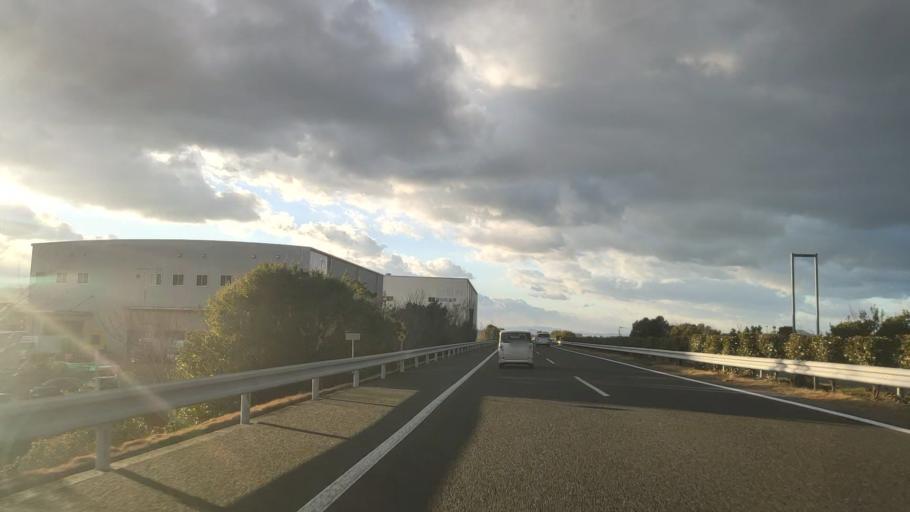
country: JP
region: Ehime
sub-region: Shikoku-chuo Shi
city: Matsuyama
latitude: 33.7863
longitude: 132.8390
